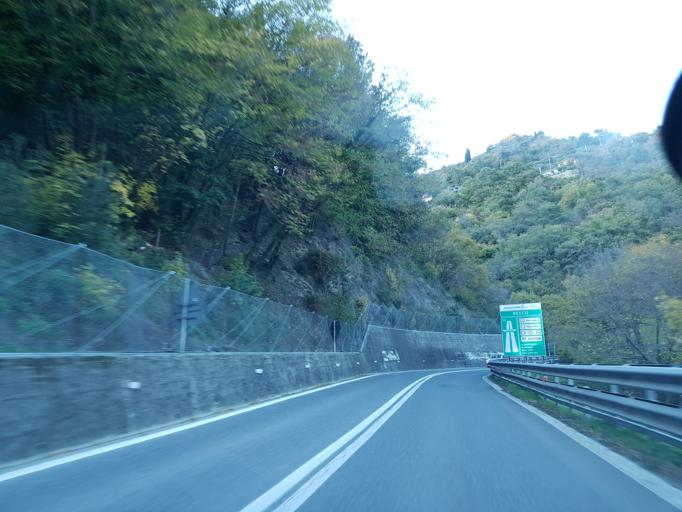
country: IT
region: Liguria
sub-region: Provincia di Genova
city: Recco
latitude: 44.3692
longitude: 9.1466
